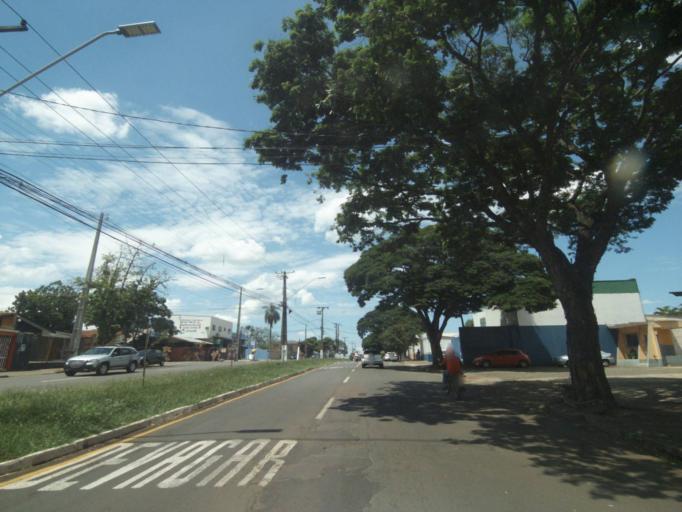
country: BR
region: Parana
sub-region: Londrina
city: Londrina
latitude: -23.3080
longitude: -51.2017
